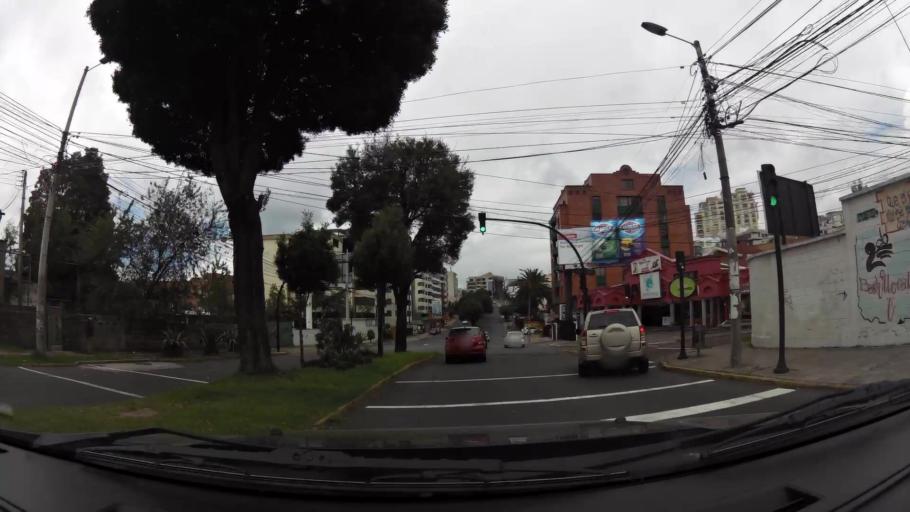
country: EC
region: Pichincha
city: Quito
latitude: -0.1630
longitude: -78.4897
